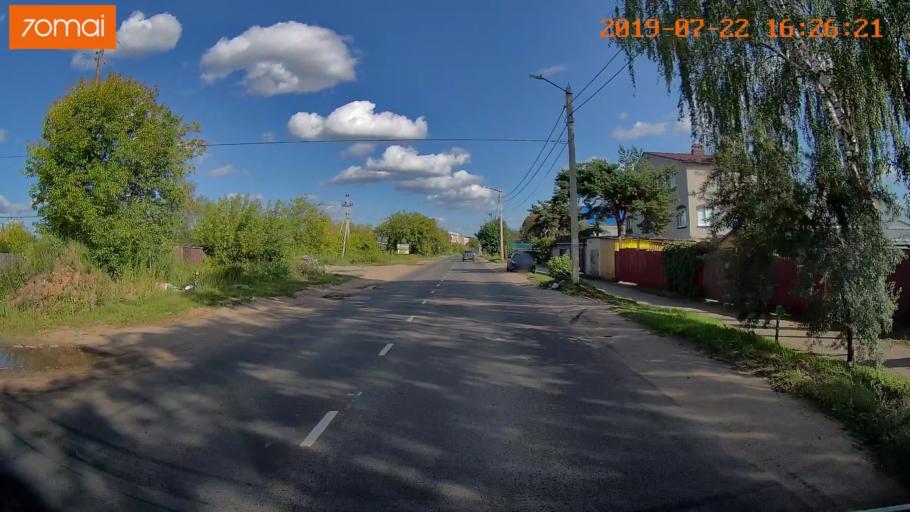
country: RU
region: Ivanovo
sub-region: Gorod Ivanovo
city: Ivanovo
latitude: 57.0494
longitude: 40.9333
